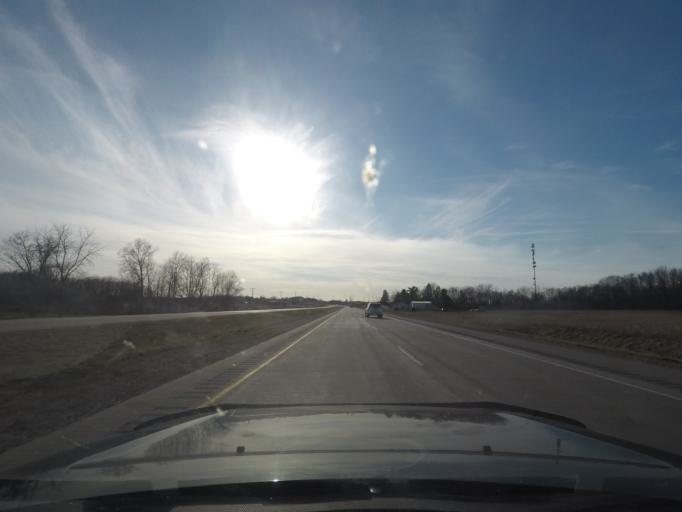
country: US
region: Indiana
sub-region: Marshall County
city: Plymouth
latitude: 41.4500
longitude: -86.3006
